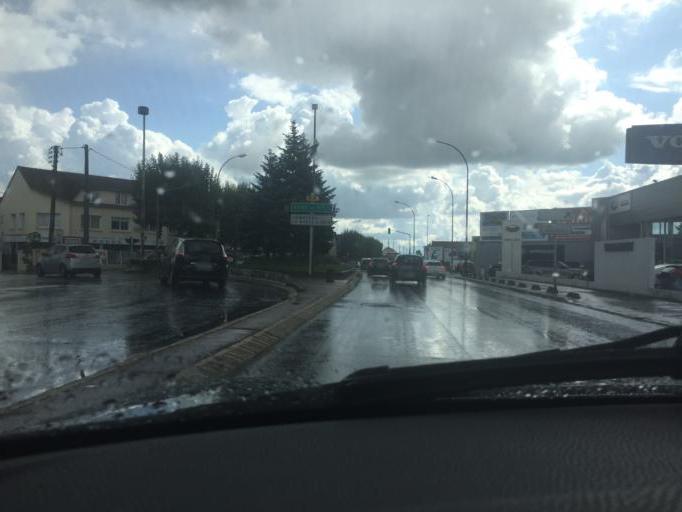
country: FR
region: Ile-de-France
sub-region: Departement du Val-de-Marne
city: Chennevieres-sur-Marne
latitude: 48.7977
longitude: 2.5470
